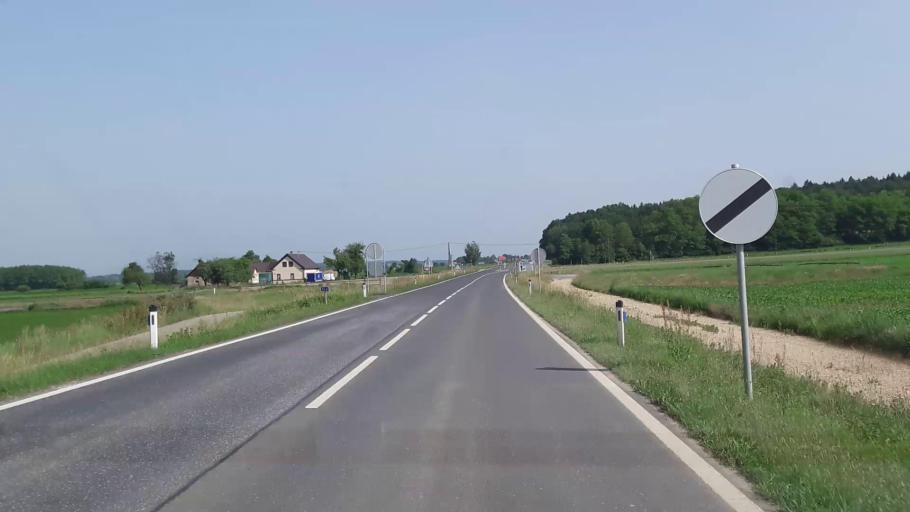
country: AT
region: Burgenland
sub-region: Politischer Bezirk Jennersdorf
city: Rudersdorf
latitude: 47.0656
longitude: 16.1144
